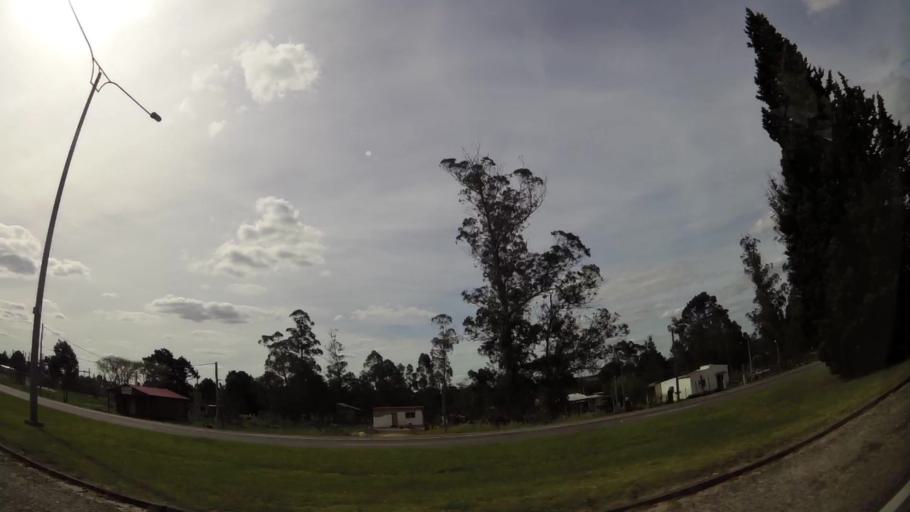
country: UY
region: Canelones
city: Empalme Olmos
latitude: -34.7814
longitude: -55.8765
